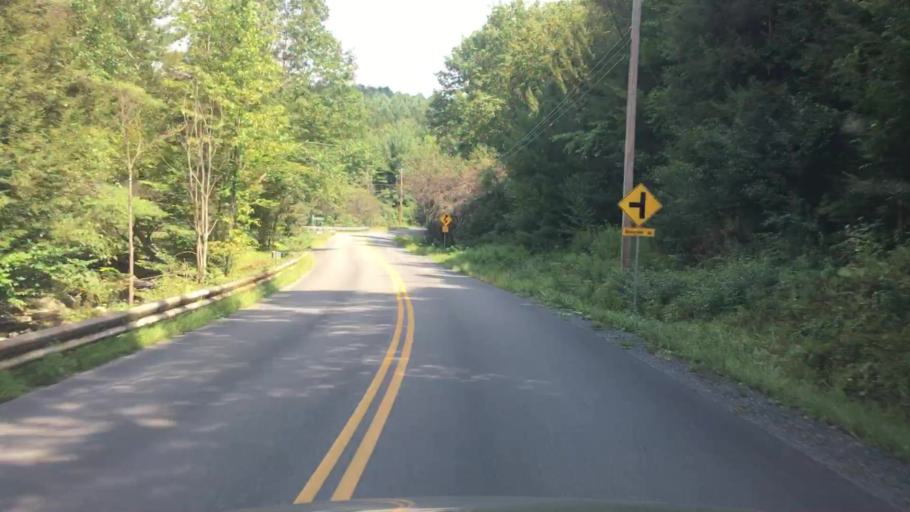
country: US
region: Vermont
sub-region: Windham County
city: West Brattleboro
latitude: 42.8055
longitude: -72.6178
